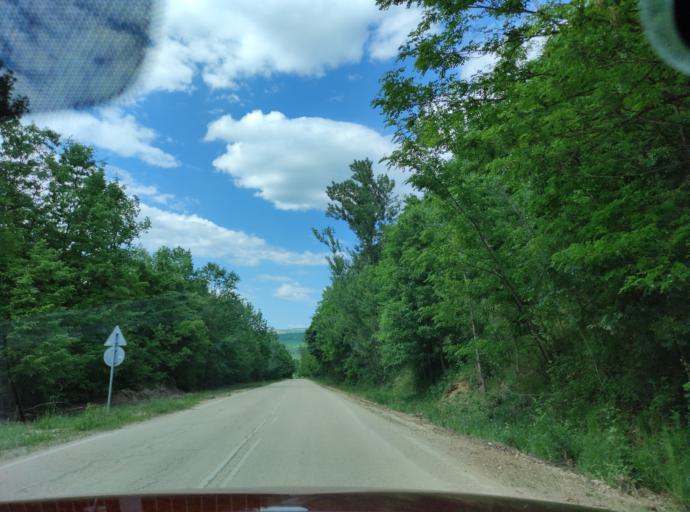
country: BG
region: Montana
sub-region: Obshtina Montana
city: Montana
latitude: 43.3880
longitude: 23.0768
